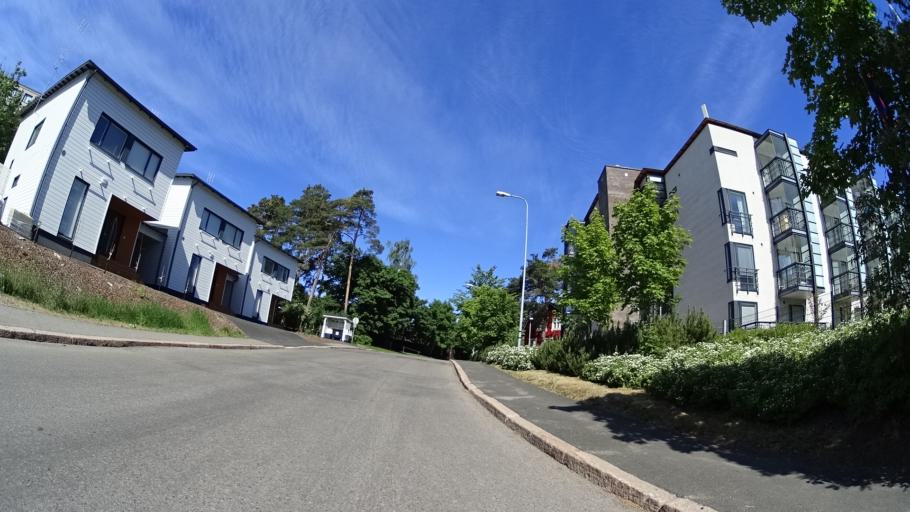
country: FI
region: Uusimaa
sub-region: Helsinki
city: Teekkarikylae
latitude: 60.2241
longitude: 24.8433
